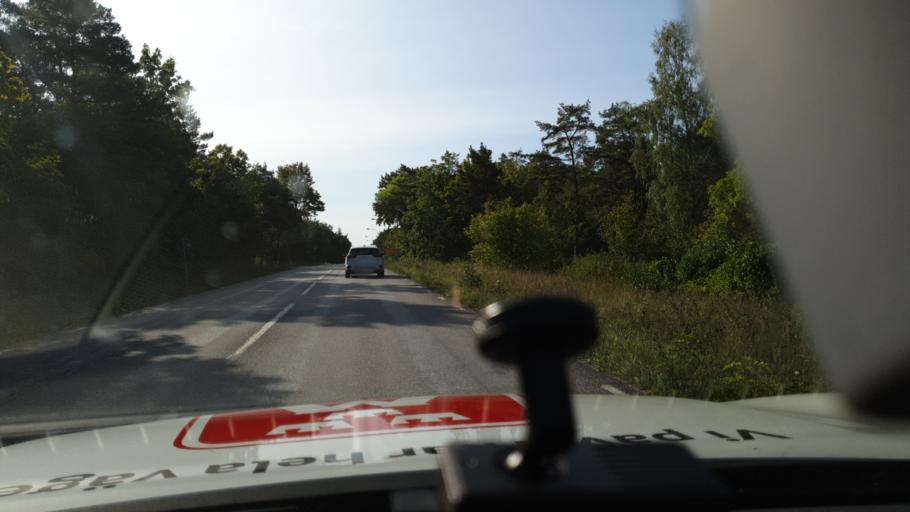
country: SE
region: Gotland
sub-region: Gotland
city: Klintehamn
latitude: 57.3374
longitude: 18.1907
